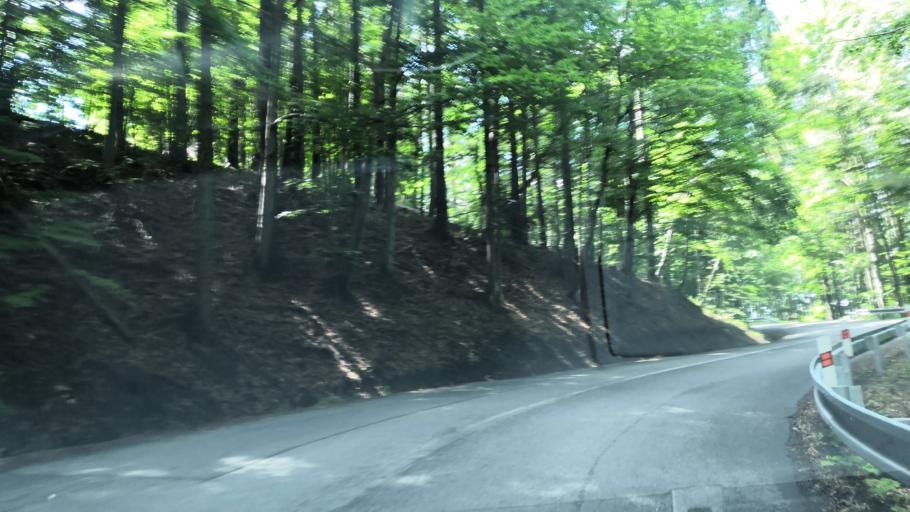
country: CZ
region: Zlin
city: Valasska Bystrice
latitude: 49.4317
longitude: 18.1311
